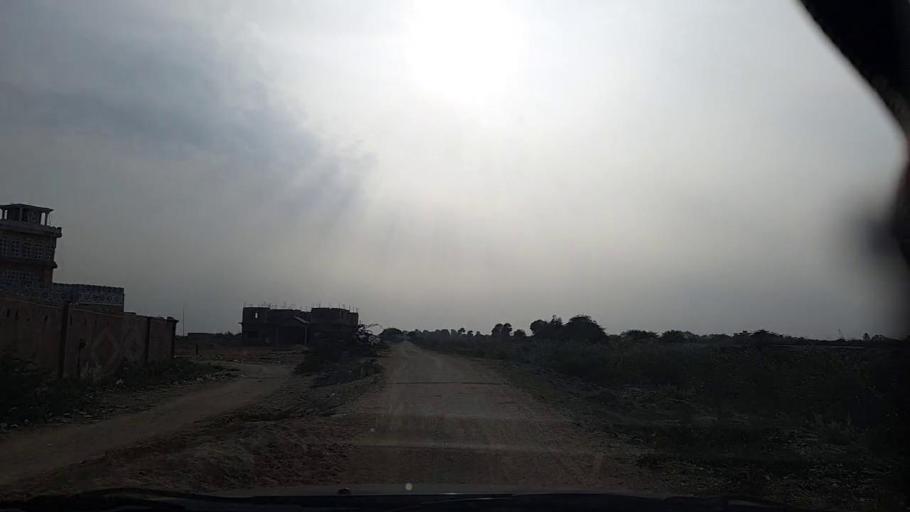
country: PK
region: Sindh
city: Thatta
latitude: 24.7109
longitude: 67.9332
